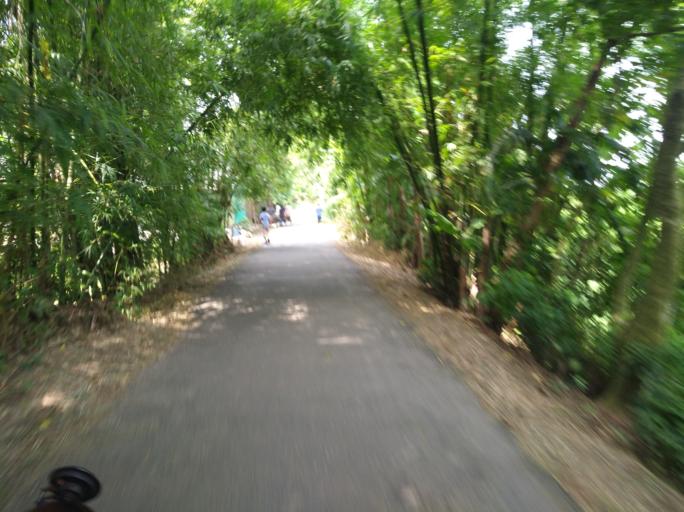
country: BD
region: Dhaka
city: Palang
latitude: 23.2495
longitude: 90.3094
